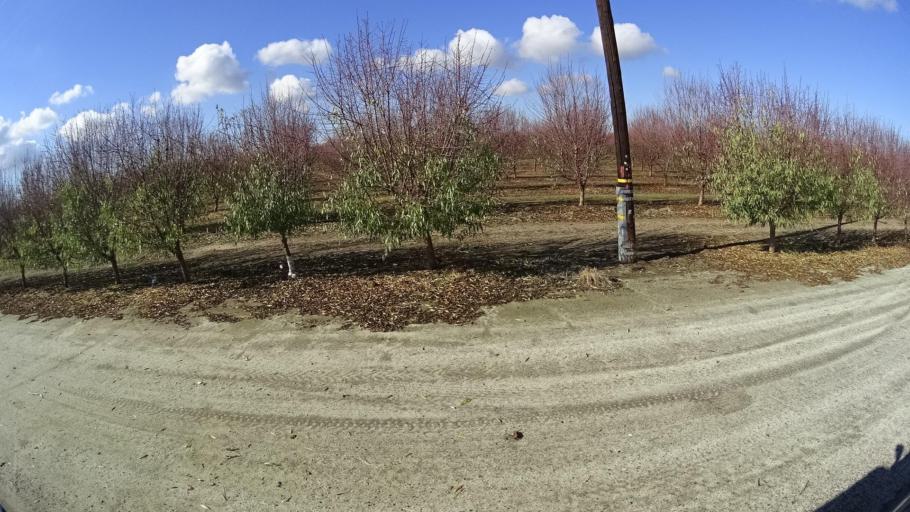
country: US
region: California
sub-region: Kern County
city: McFarland
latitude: 35.6644
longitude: -119.2588
